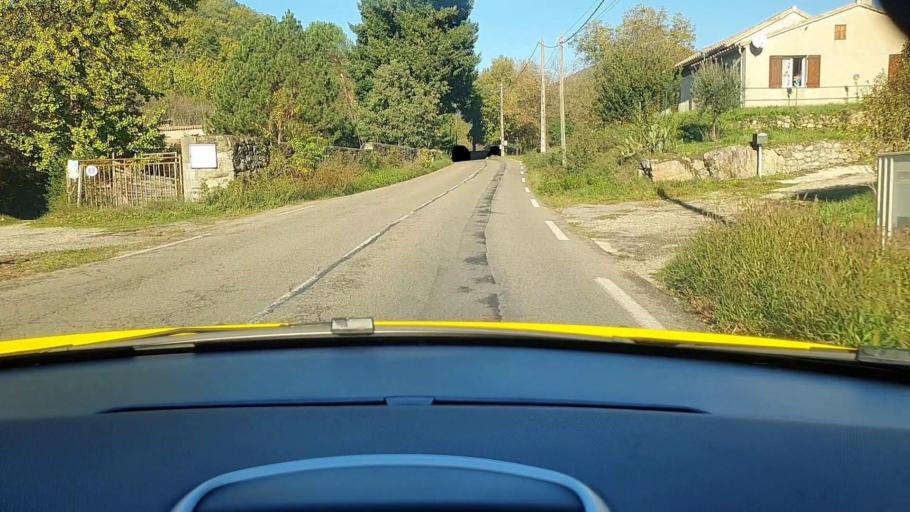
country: FR
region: Languedoc-Roussillon
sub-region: Departement du Gard
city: Le Vigan
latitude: 43.9849
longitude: 3.5835
